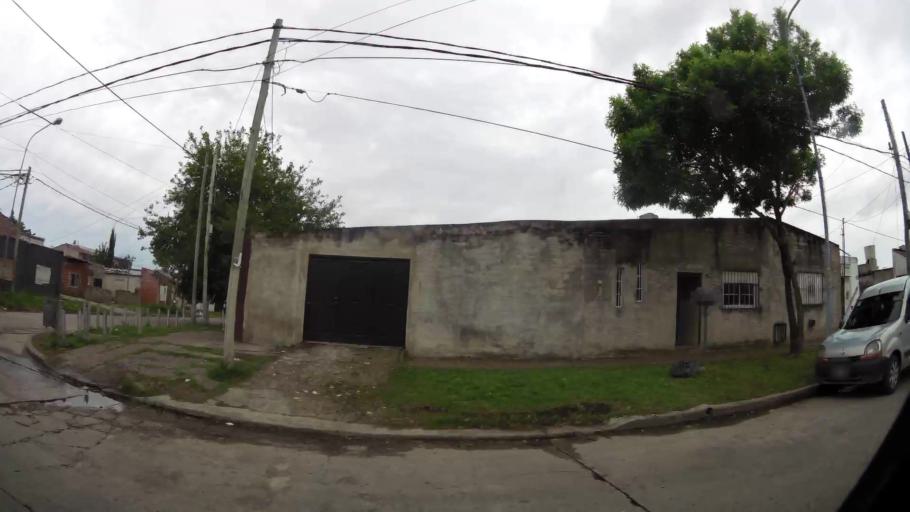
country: AR
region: Buenos Aires
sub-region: Partido de Lanus
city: Lanus
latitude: -34.7245
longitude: -58.3729
